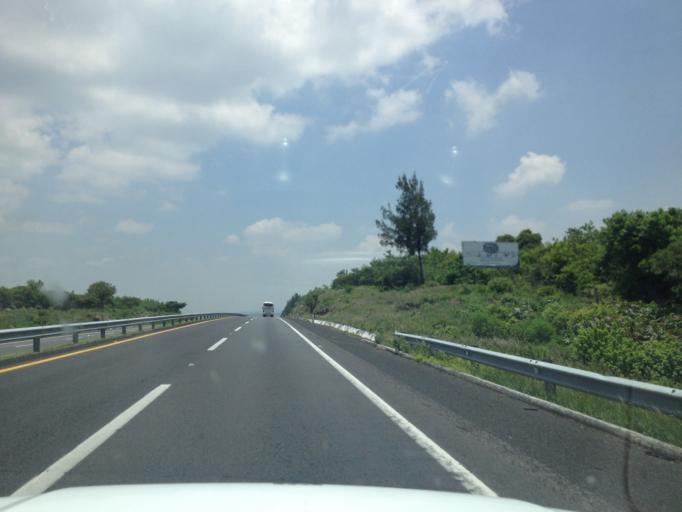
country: MX
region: Michoacan
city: Churintzio
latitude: 20.1105
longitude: -102.0407
